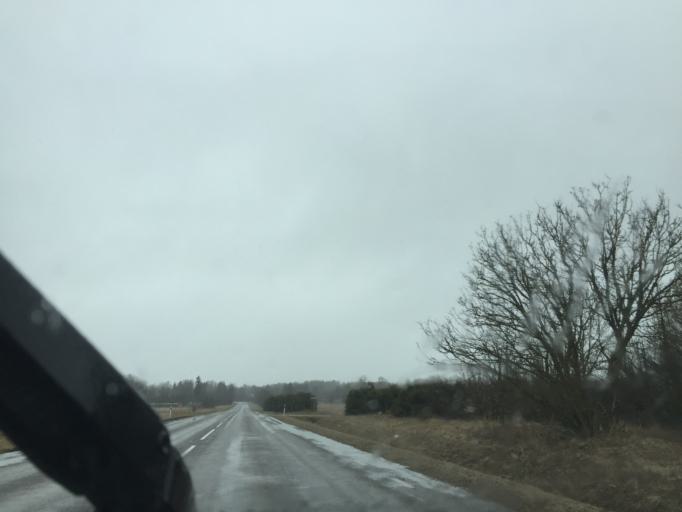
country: EE
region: Laeaene
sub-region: Ridala Parish
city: Uuemoisa
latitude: 58.8833
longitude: 23.6017
